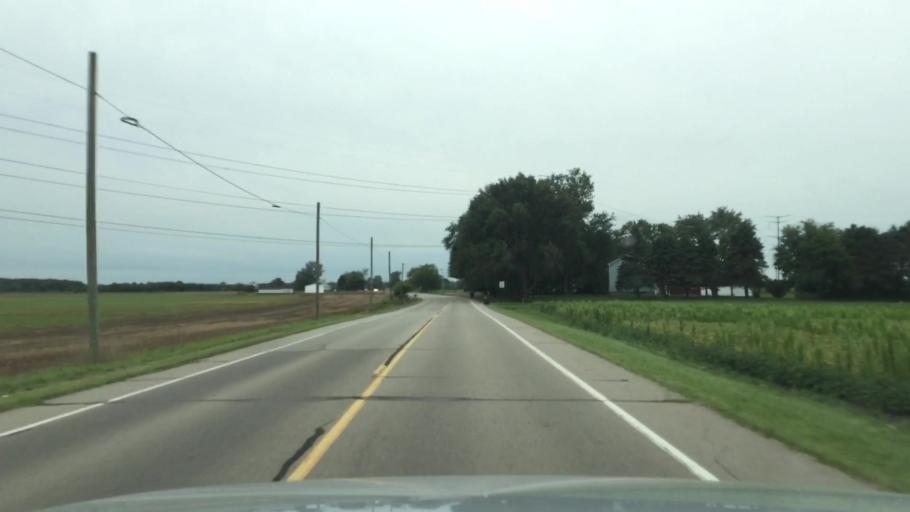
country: US
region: Michigan
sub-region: Washtenaw County
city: Milan
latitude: 42.1213
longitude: -83.7026
